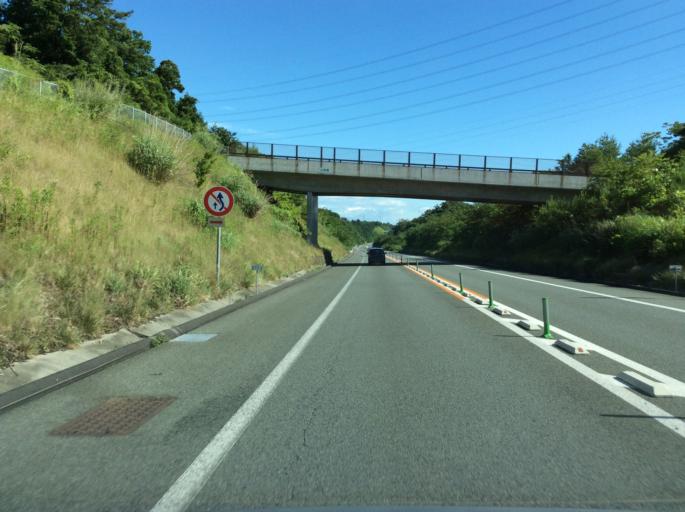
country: JP
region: Fukushima
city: Namie
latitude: 37.3161
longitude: 140.9923
